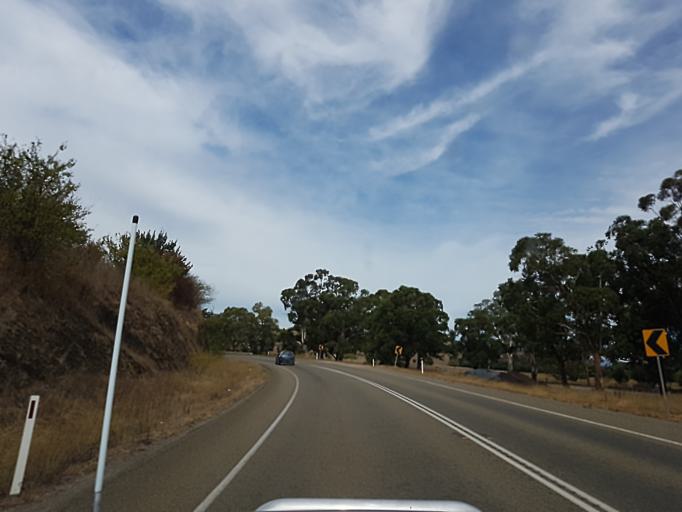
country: AU
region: Victoria
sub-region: Murrindindi
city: Alexandra
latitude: -37.2119
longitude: 145.4382
